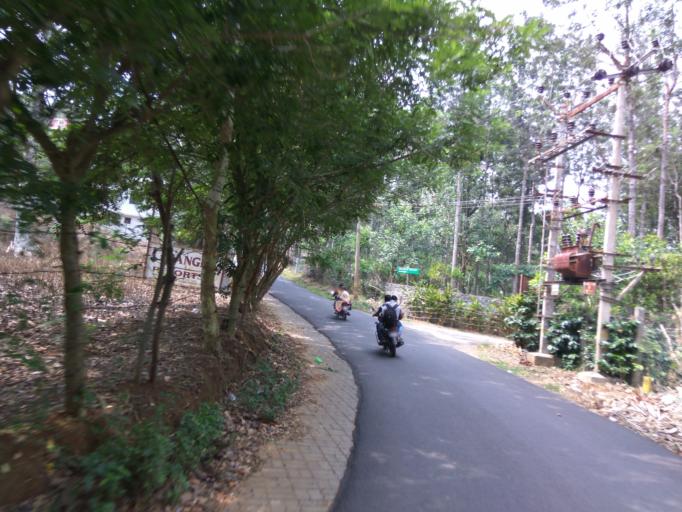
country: IN
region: Tamil Nadu
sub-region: Salem
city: Salem
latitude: 11.7750
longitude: 78.2194
